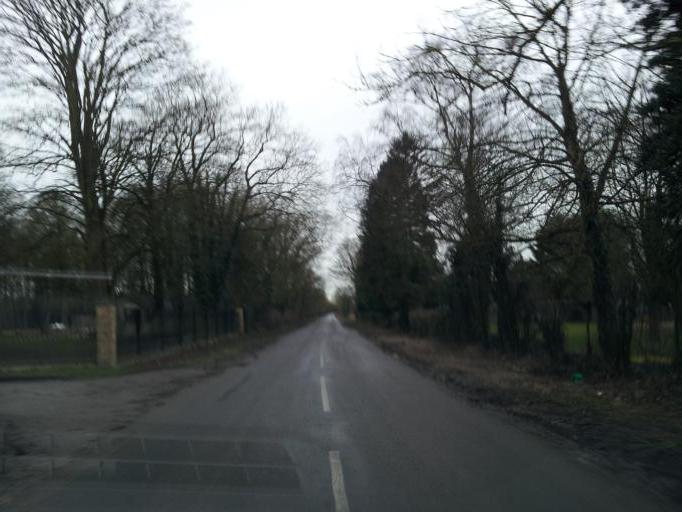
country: GB
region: England
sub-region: Cambridgeshire
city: Fulbourn
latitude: 52.1906
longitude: 0.2406
